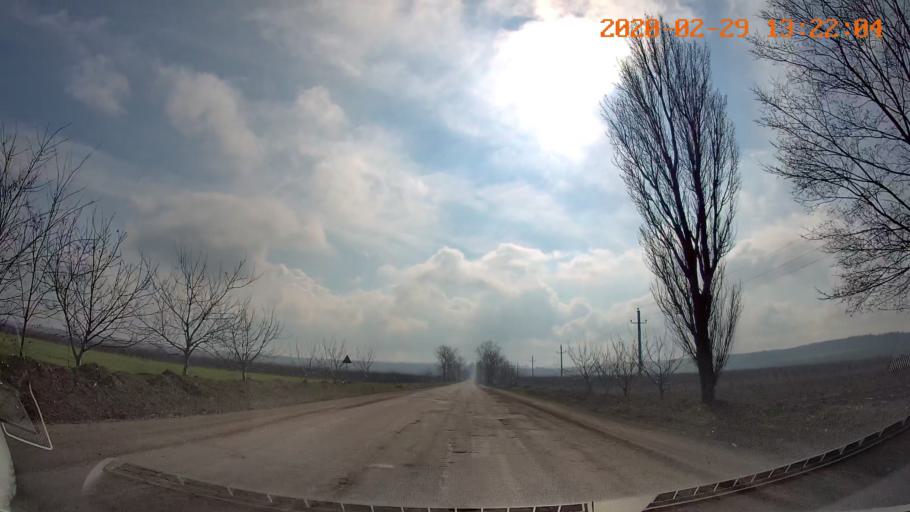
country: MD
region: Telenesti
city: Camenca
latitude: 47.9646
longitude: 28.6286
